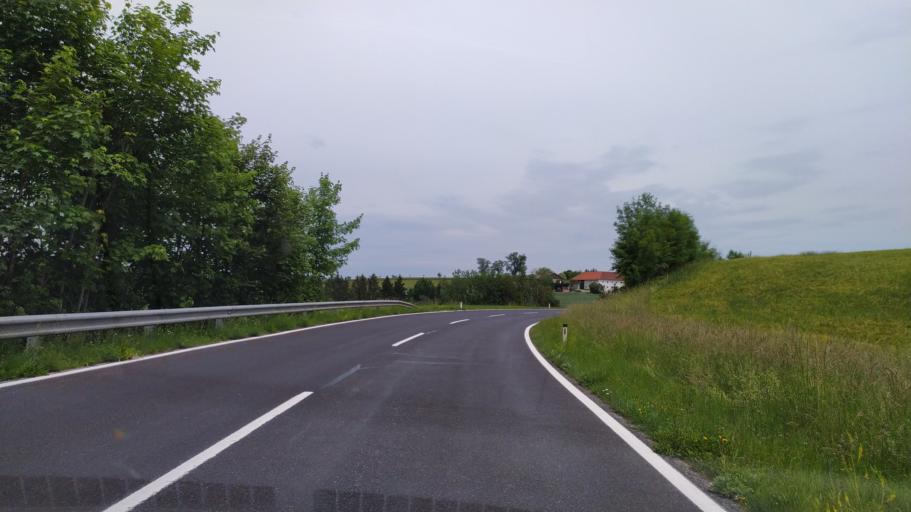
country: AT
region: Lower Austria
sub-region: Politischer Bezirk Amstetten
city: Strengberg
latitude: 48.1360
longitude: 14.6084
